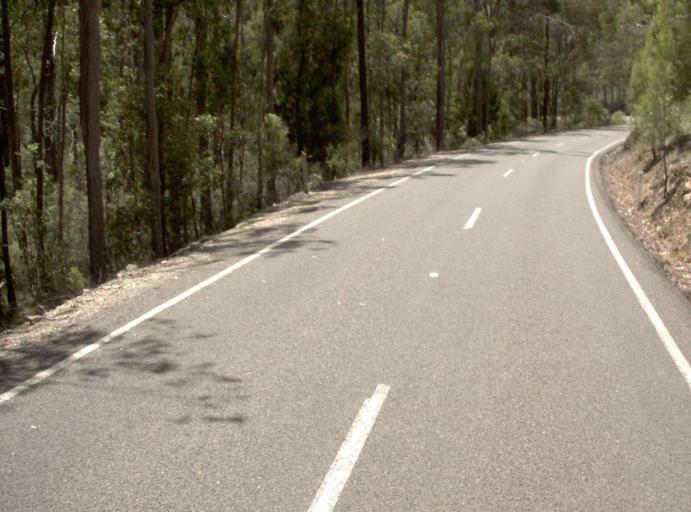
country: AU
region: Victoria
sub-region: East Gippsland
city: Lakes Entrance
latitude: -37.5857
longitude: 147.8937
